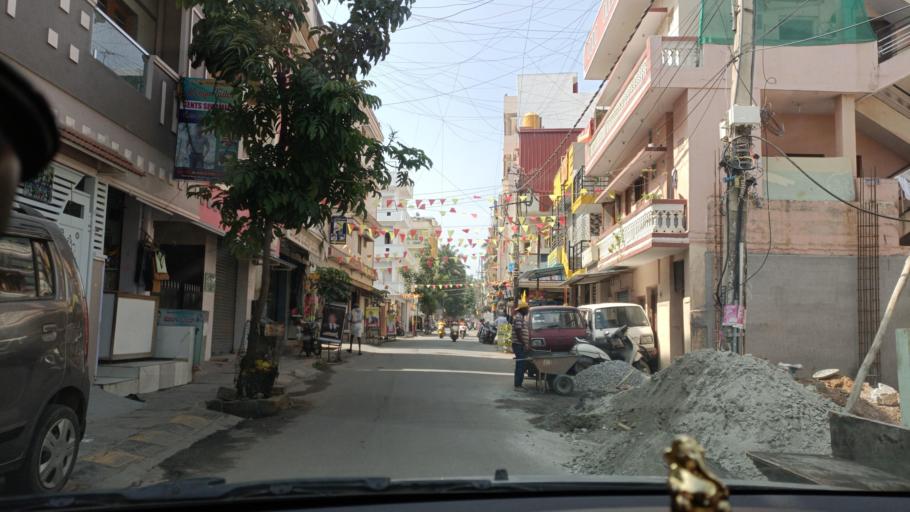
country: IN
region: Karnataka
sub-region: Bangalore Urban
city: Bangalore
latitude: 12.9174
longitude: 77.6176
